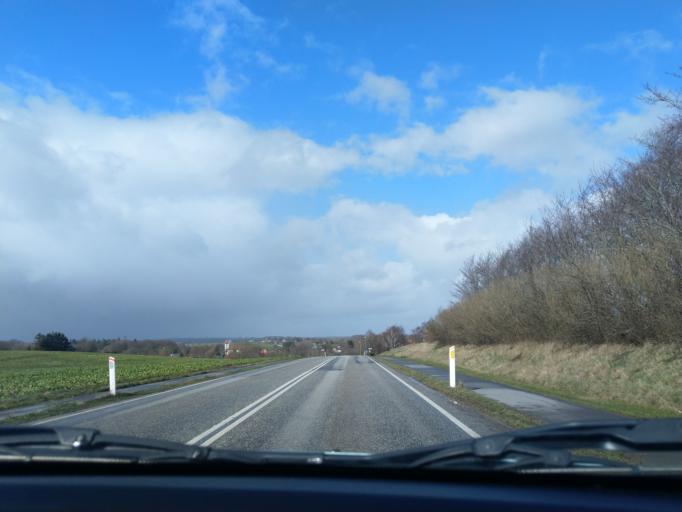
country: DK
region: Zealand
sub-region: Naestved Kommune
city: Naestved
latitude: 55.3111
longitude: 11.6850
